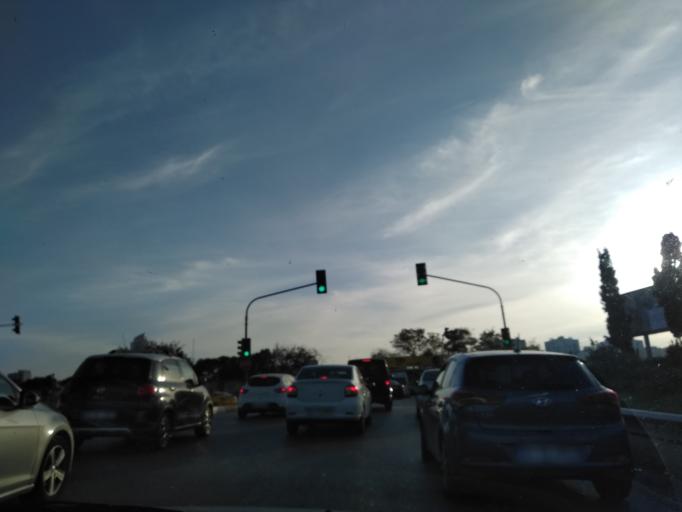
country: TR
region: Istanbul
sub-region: Atasehir
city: Atasehir
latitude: 40.9813
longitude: 29.1000
